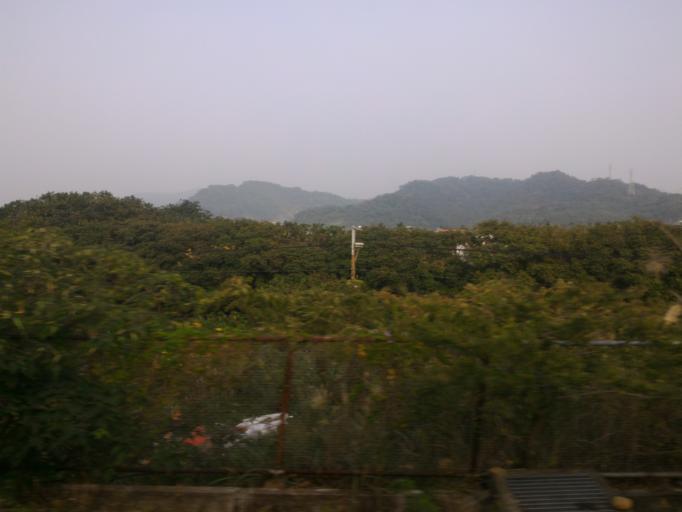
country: TW
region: Taiwan
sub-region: Taoyuan
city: Taoyuan
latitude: 24.9629
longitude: 121.3381
